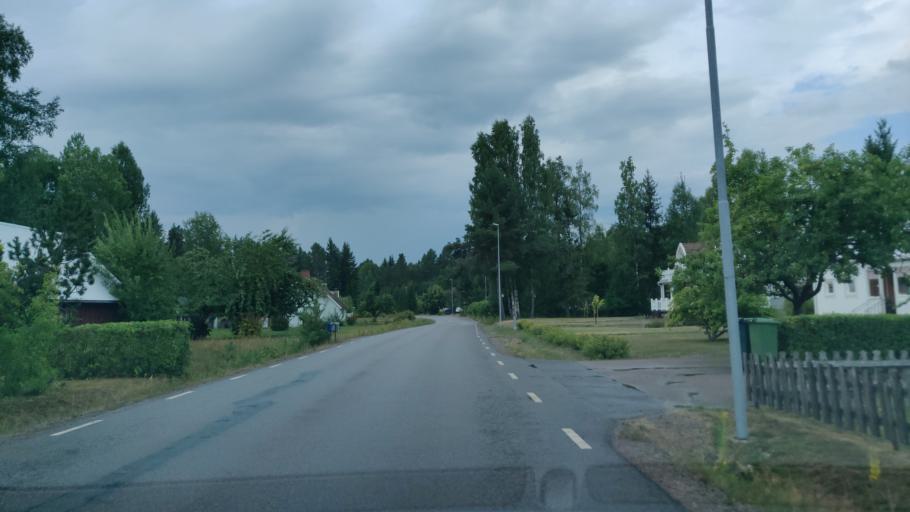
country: SE
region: Vaermland
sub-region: Munkfors Kommun
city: Munkfors
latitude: 59.8601
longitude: 13.5503
